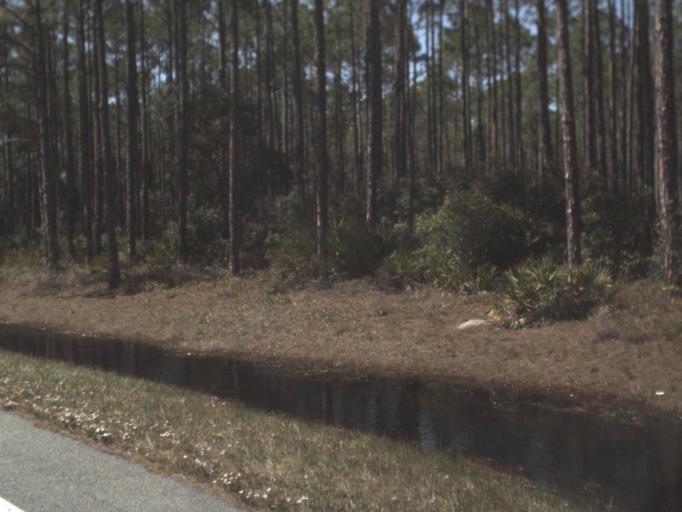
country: US
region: Florida
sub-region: Franklin County
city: Carrabelle
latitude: 29.9196
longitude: -84.5023
